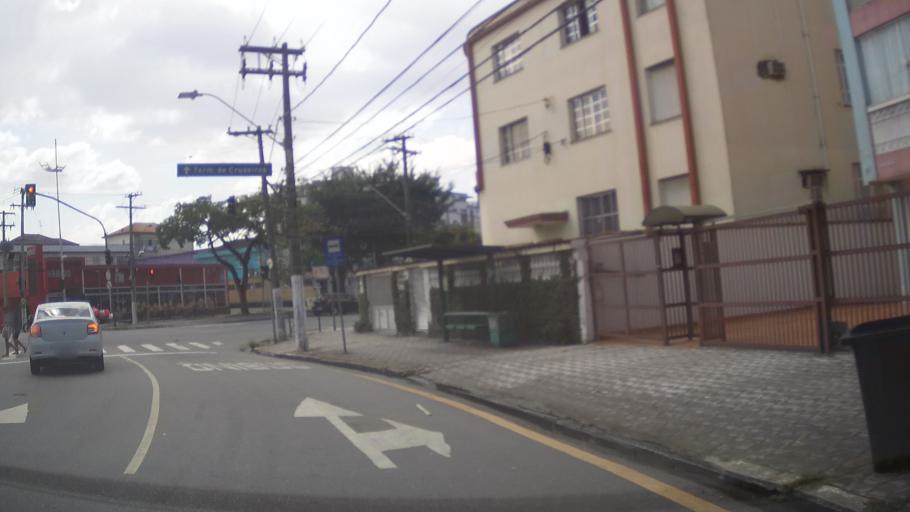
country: BR
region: Sao Paulo
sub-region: Santos
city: Santos
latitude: -23.9617
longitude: -46.3165
